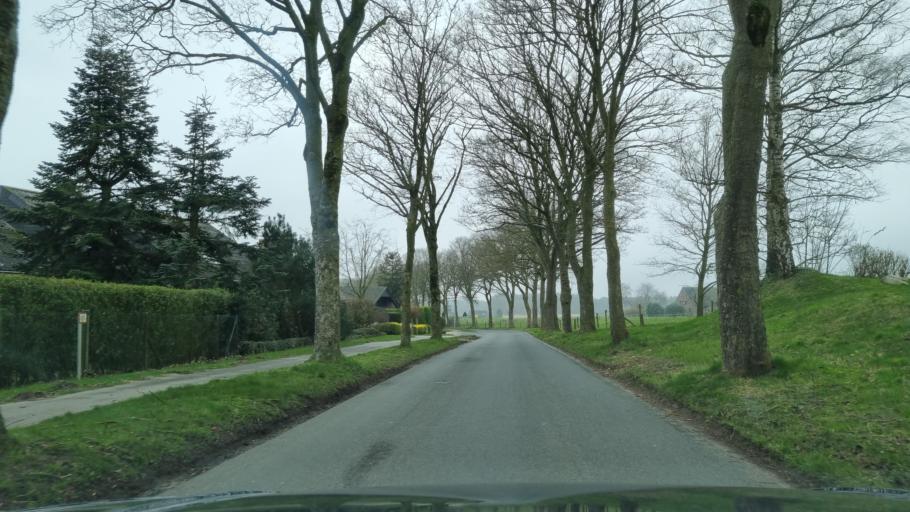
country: DE
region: North Rhine-Westphalia
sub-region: Regierungsbezirk Dusseldorf
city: Kleve
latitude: 51.7741
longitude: 6.1015
